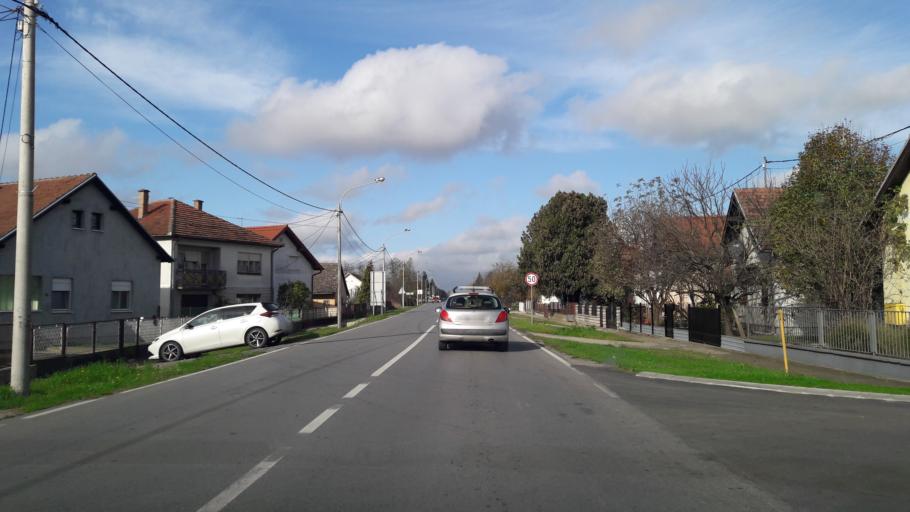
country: HR
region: Osjecko-Baranjska
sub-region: Grad Osijek
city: Bilje
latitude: 45.6086
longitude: 18.7411
